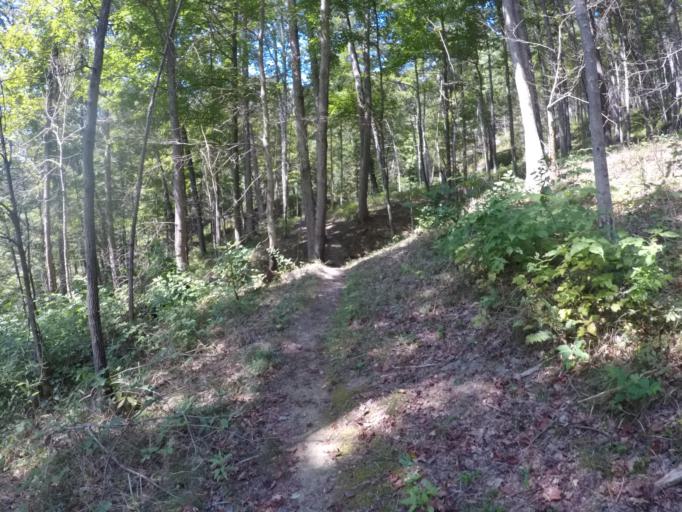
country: US
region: Ohio
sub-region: Lawrence County
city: Ironton
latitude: 38.6219
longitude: -82.6231
